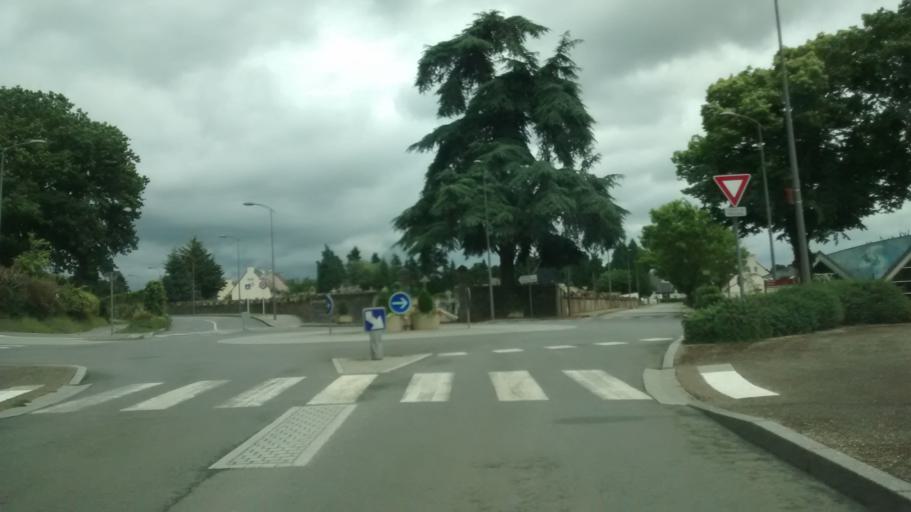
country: FR
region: Brittany
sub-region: Departement du Morbihan
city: Carentoir
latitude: 47.8180
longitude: -2.1331
